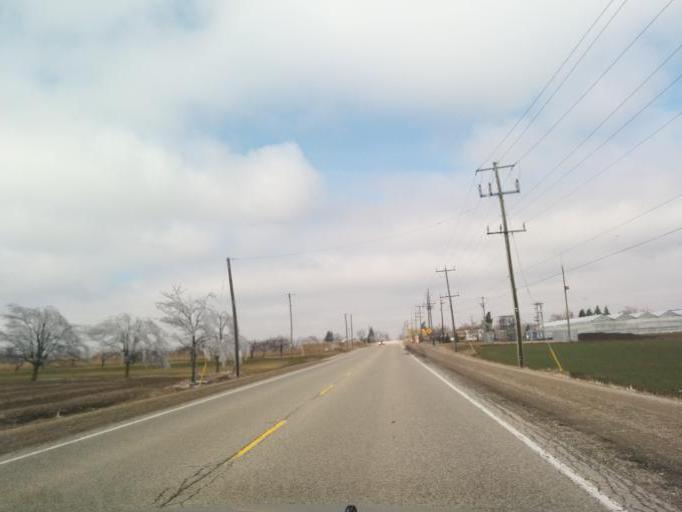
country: CA
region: Ontario
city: Waterloo
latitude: 43.6297
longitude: -80.5505
